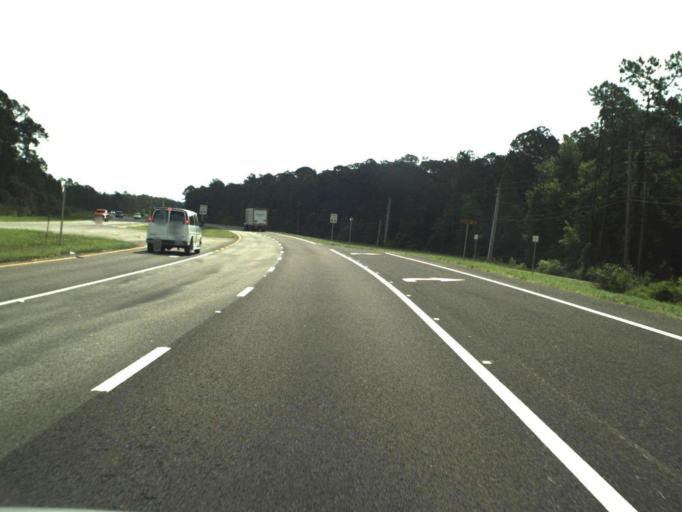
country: US
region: Florida
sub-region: Volusia County
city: Lake Helen
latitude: 29.0209
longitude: -81.2052
